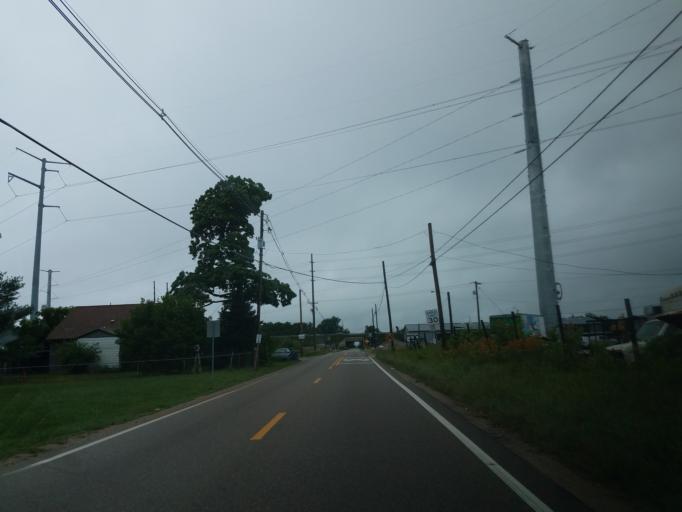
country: US
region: Illinois
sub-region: McLean County
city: Bloomington
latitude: 40.4569
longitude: -88.9815
